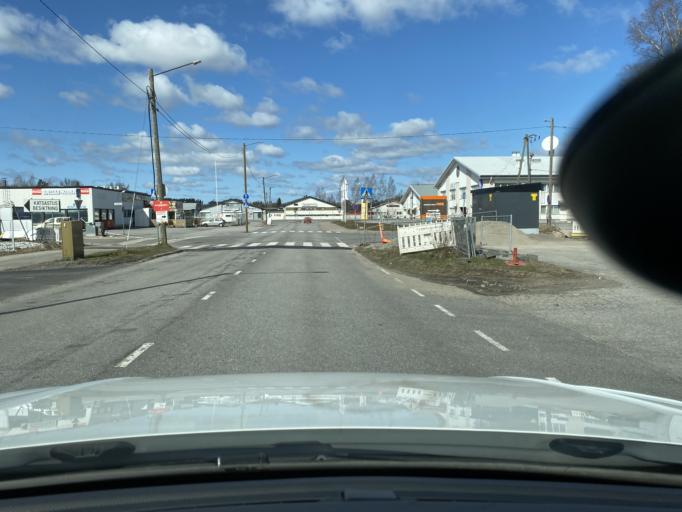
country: FI
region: Varsinais-Suomi
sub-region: Turku
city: Turku
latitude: 60.4825
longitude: 22.3131
